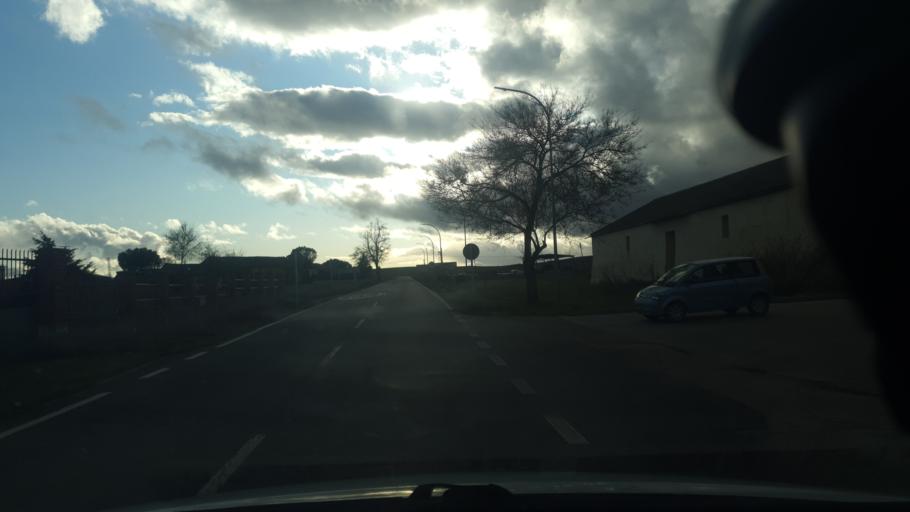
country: ES
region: Castille and Leon
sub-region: Provincia de Segovia
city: Santiuste de San Juan Bautista
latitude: 41.1539
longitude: -4.5730
